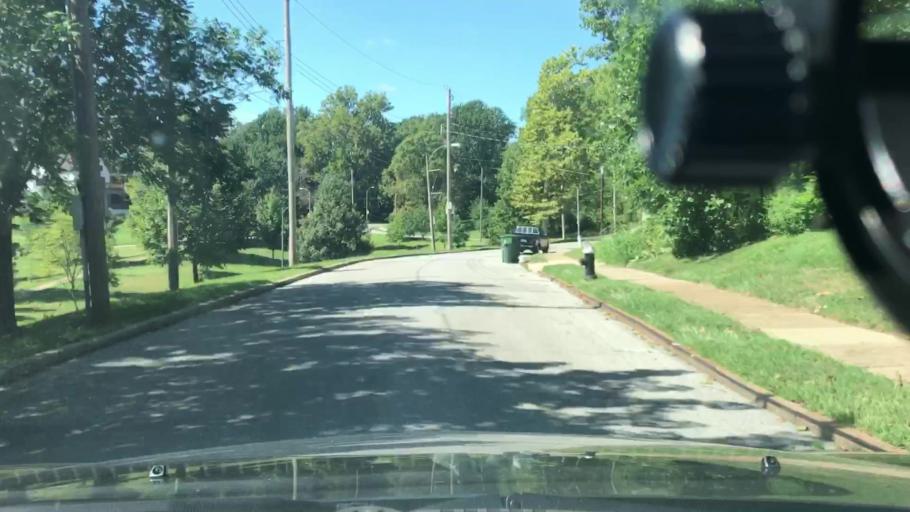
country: US
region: Missouri
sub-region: Saint Louis County
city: Richmond Heights
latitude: 38.6147
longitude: -90.2919
